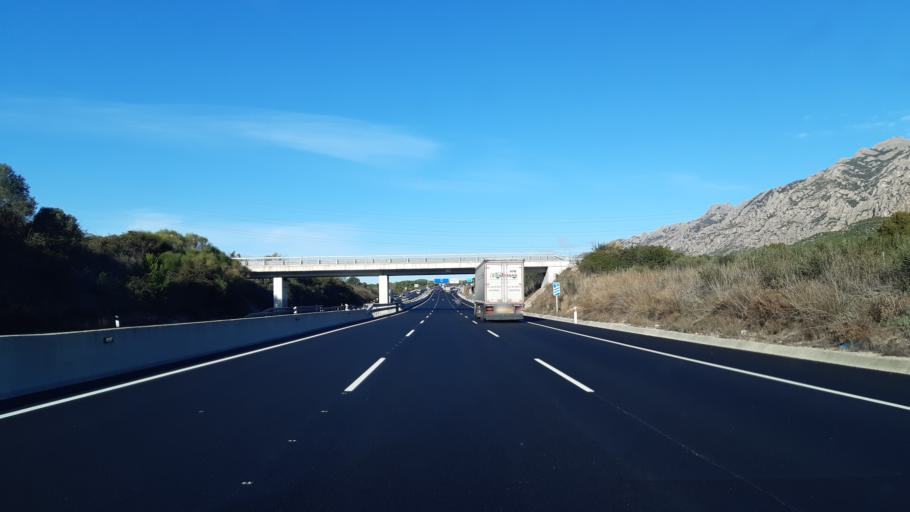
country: ES
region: Catalonia
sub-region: Provincia de Barcelona
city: Collbato
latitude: 41.5520
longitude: 1.8434
